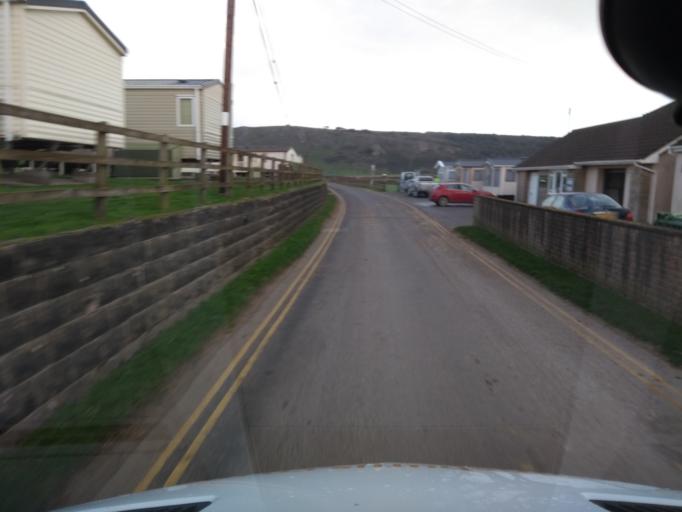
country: GB
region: England
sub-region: North Somerset
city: Weston-super-Mare
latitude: 51.3190
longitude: -3.0100
